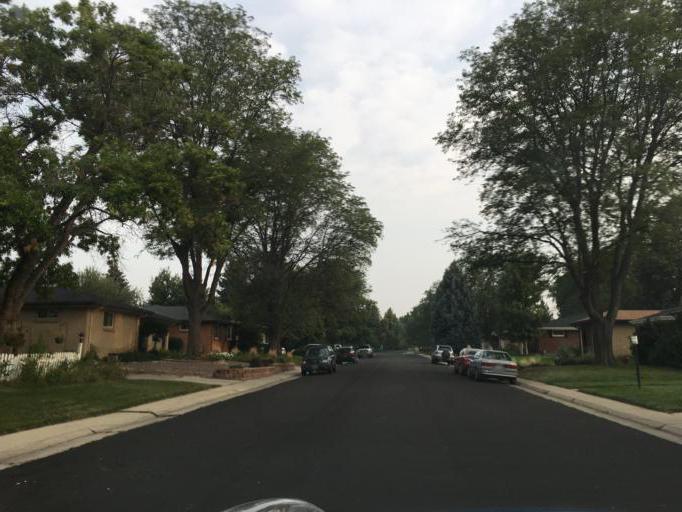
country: US
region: Colorado
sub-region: Arapahoe County
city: Glendale
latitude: 39.6873
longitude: -104.9254
